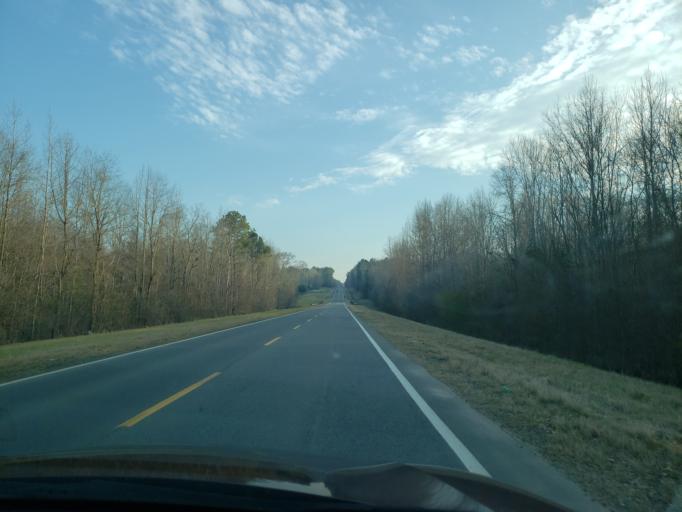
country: US
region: Alabama
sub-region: Hale County
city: Greensboro
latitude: 32.7625
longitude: -87.5854
